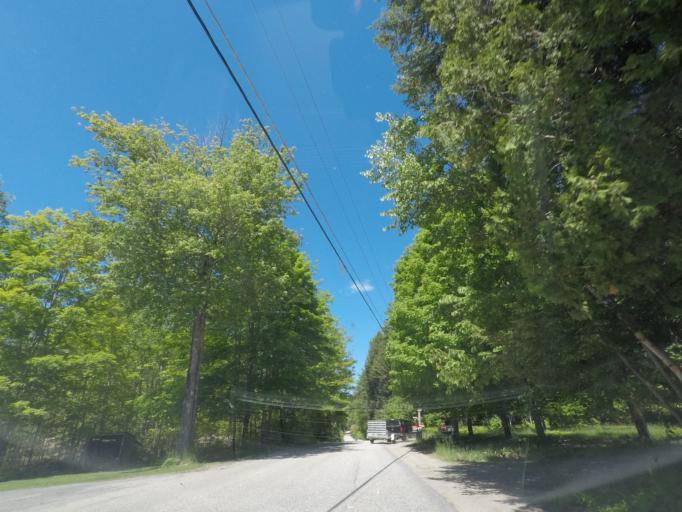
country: US
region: Maine
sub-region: Kennebec County
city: Winthrop
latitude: 44.2642
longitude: -69.9155
